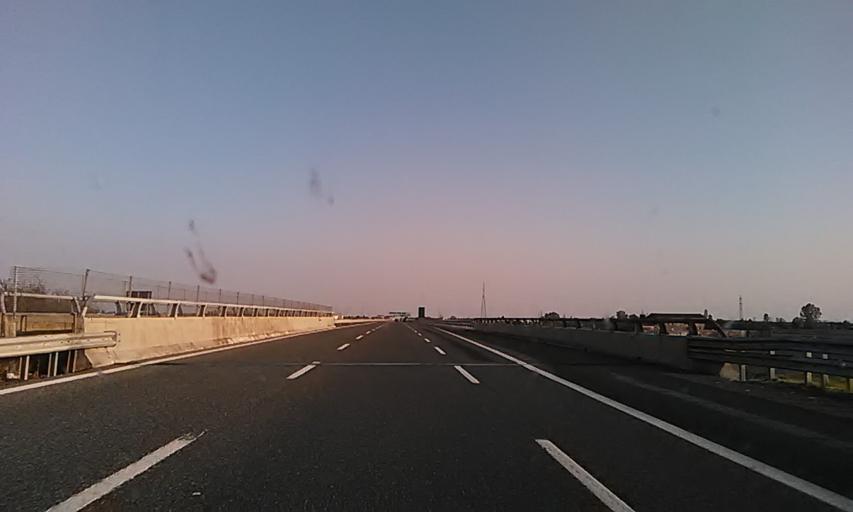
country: IT
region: Piedmont
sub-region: Provincia di Novara
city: Vicolungo
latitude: 45.4759
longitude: 8.4466
